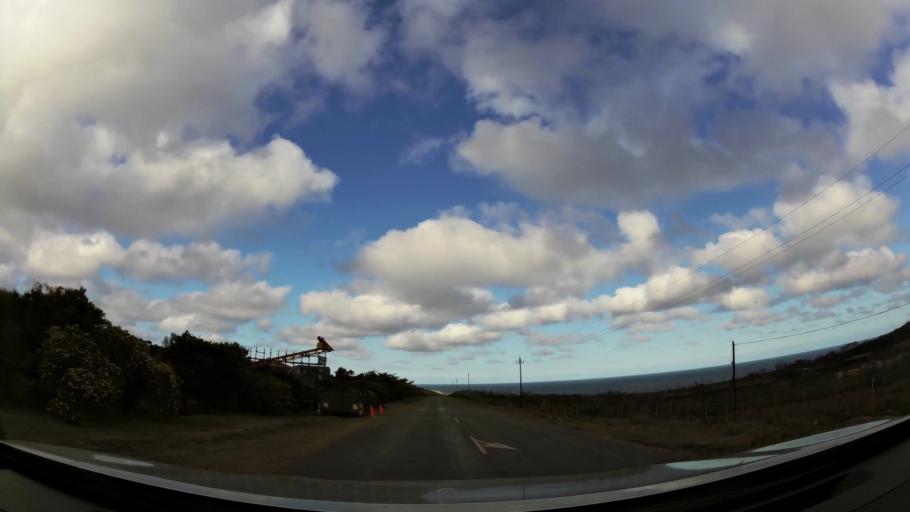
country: ZA
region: Western Cape
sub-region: Eden District Municipality
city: Plettenberg Bay
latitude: -34.0948
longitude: 23.3636
